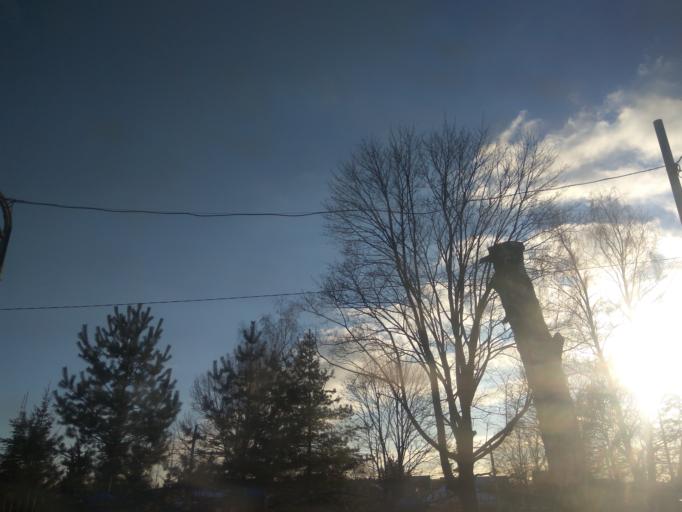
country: RU
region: Moskovskaya
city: Bykovo
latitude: 55.6562
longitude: 38.1012
